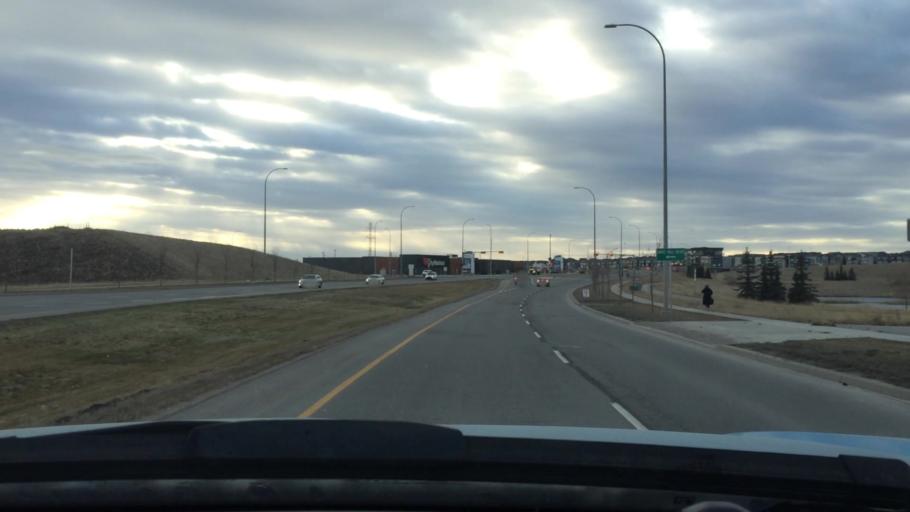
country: CA
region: Alberta
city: Calgary
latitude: 51.1723
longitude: -114.1544
